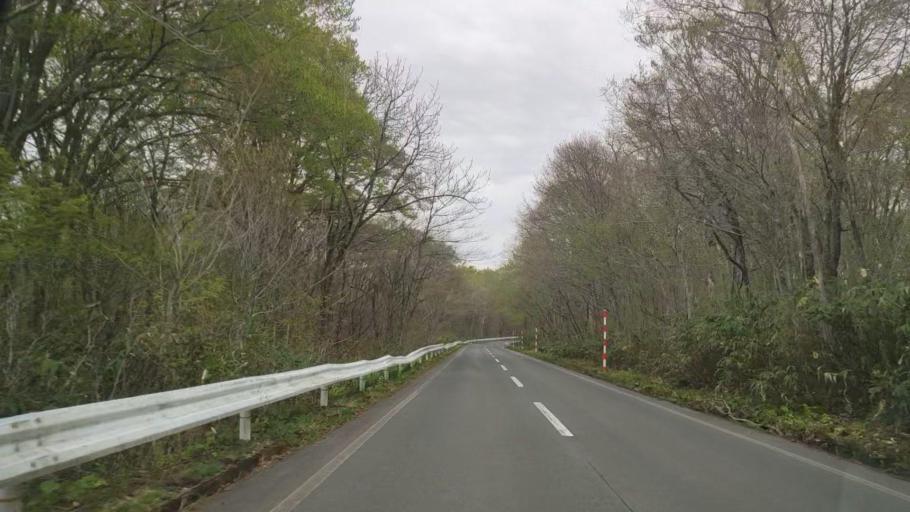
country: JP
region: Akita
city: Hanawa
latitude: 40.4031
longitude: 140.8071
